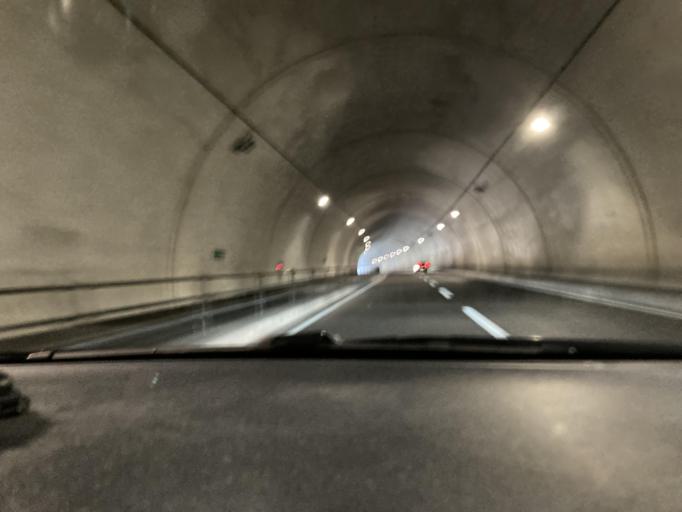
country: JP
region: Okinawa
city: Naha-shi
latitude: 26.2030
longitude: 127.7108
